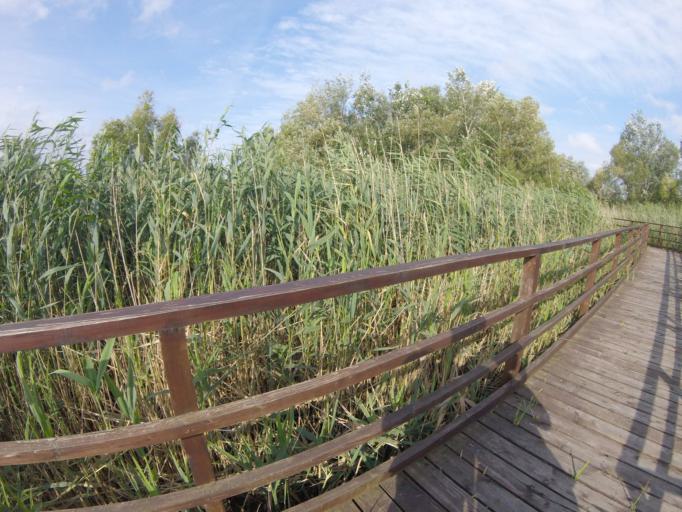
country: HU
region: Hajdu-Bihar
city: Hortobagy
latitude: 47.6055
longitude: 21.0705
